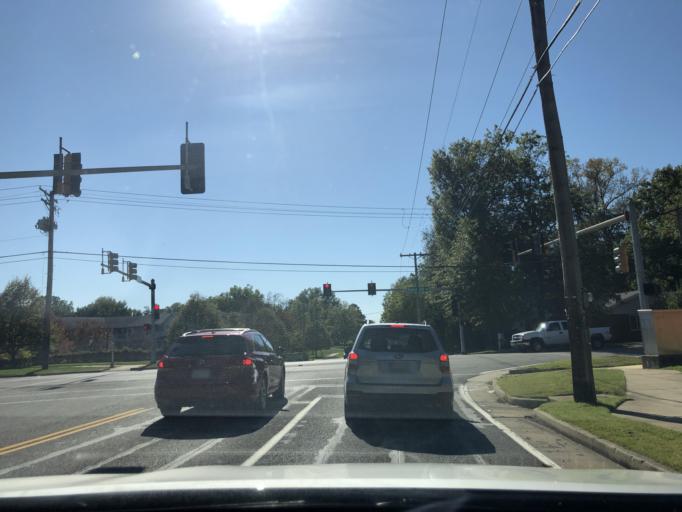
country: US
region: Missouri
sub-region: Saint Louis County
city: Concord
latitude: 38.4868
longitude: -90.3647
